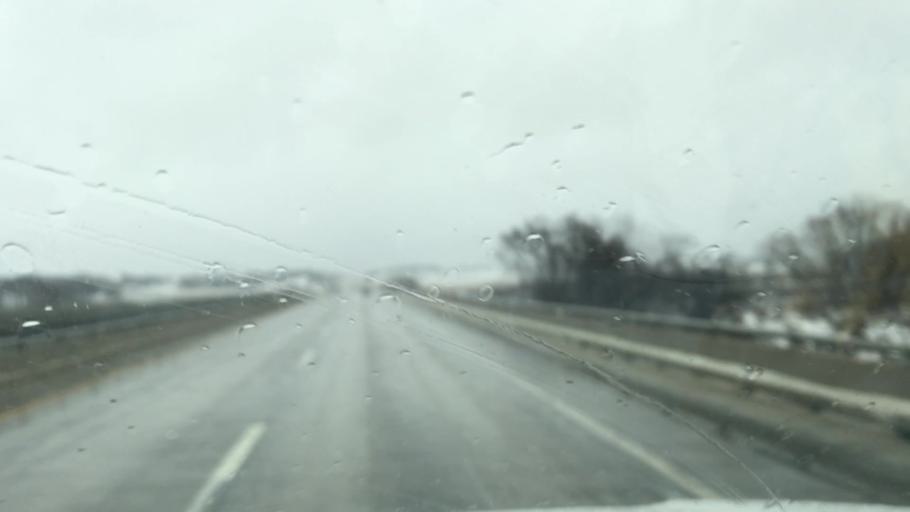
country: US
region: Missouri
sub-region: Buchanan County
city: Saint Joseph
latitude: 39.7478
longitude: -94.7269
